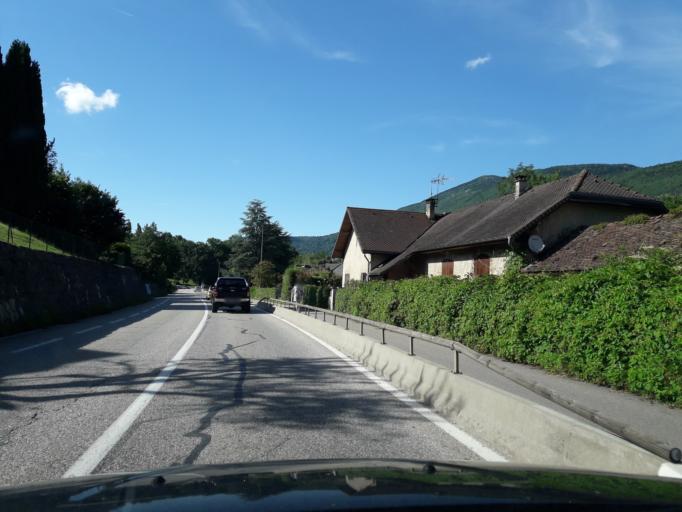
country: FR
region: Rhone-Alpes
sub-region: Departement de la Savoie
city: Novalaise
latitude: 45.5656
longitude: 5.7947
